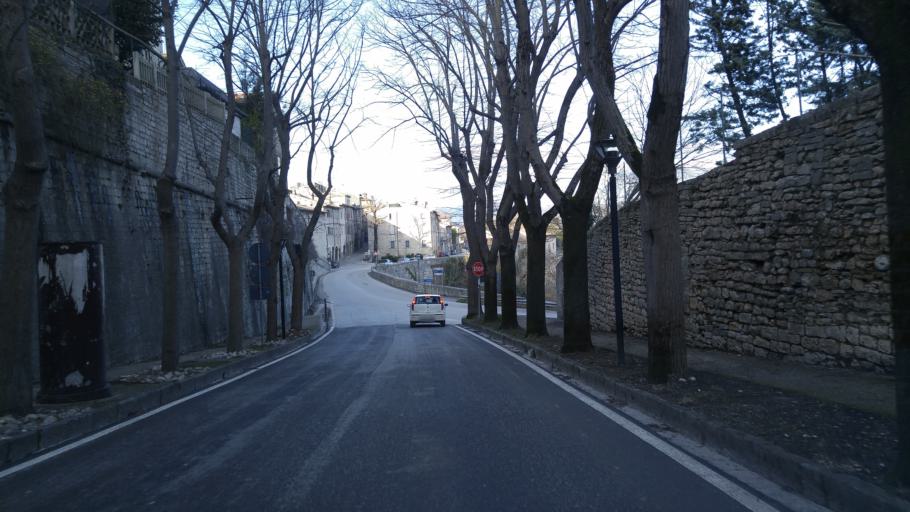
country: IT
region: The Marches
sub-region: Provincia di Pesaro e Urbino
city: Cagli
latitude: 43.5437
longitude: 12.6492
